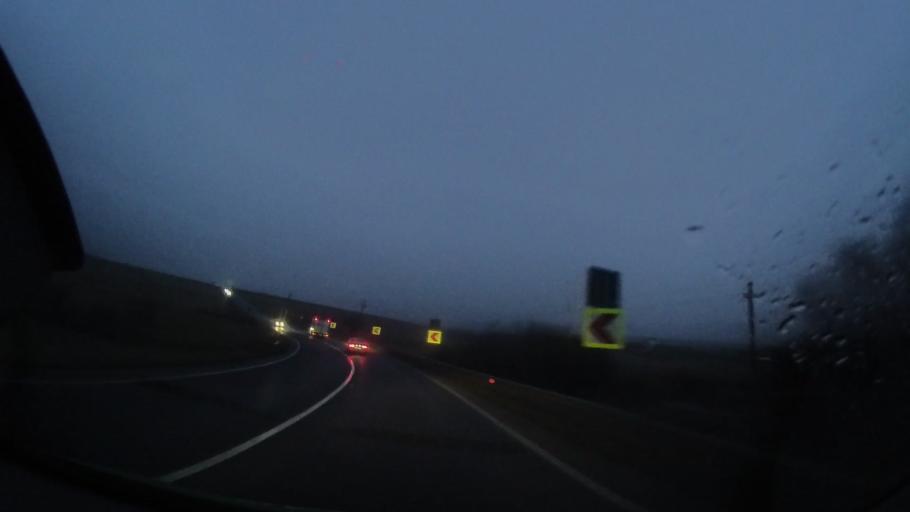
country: RO
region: Harghita
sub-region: Comuna Ditrau
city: Ditrau
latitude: 46.8271
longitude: 25.4920
